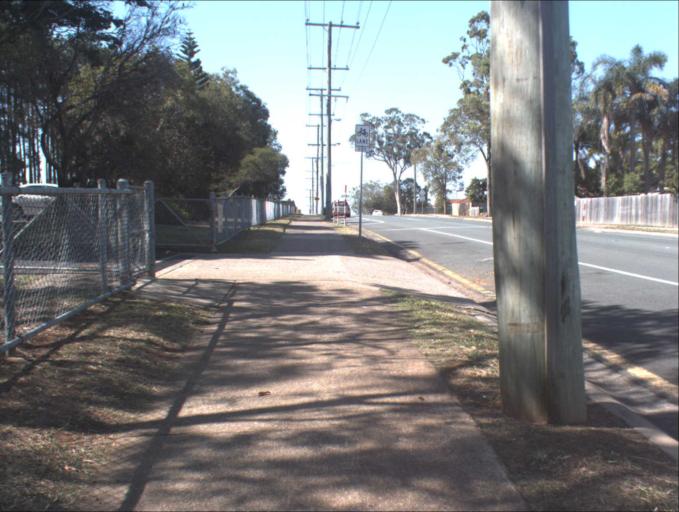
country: AU
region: Queensland
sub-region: Logan
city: Beenleigh
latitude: -27.6925
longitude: 153.2148
